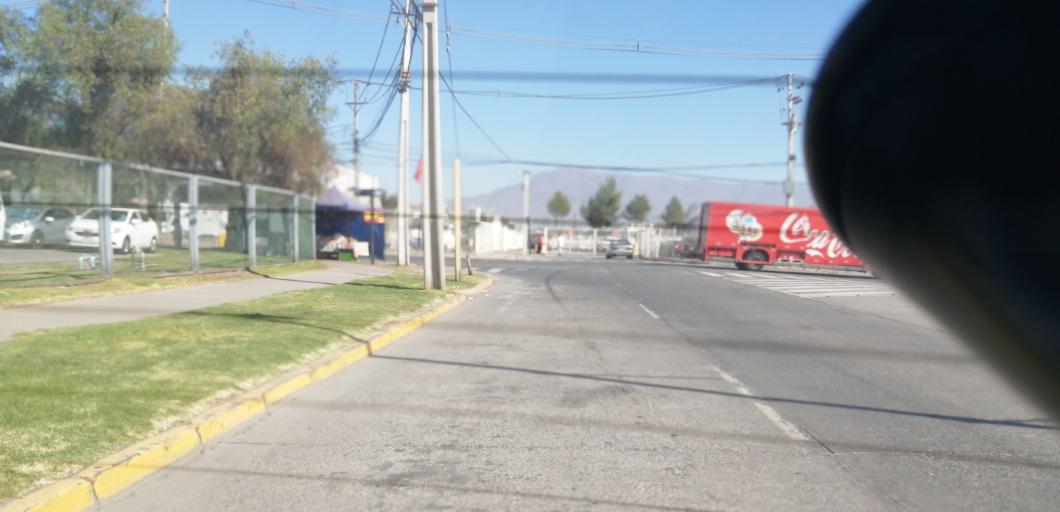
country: CL
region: Santiago Metropolitan
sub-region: Provincia de Santiago
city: Lo Prado
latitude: -33.4458
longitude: -70.7835
